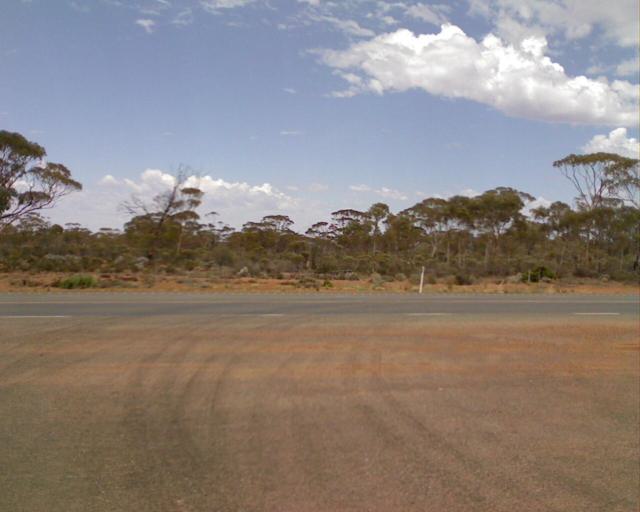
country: AU
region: Western Australia
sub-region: Kalgoorlie/Boulder
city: Stoneville
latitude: -31.1963
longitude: 121.6502
